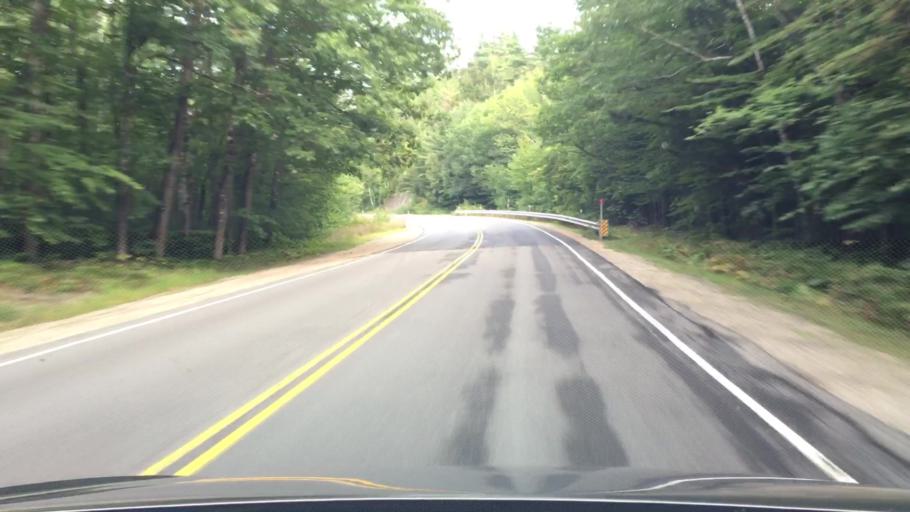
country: US
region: New Hampshire
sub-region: Carroll County
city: Conway
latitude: 44.0011
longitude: -71.2364
